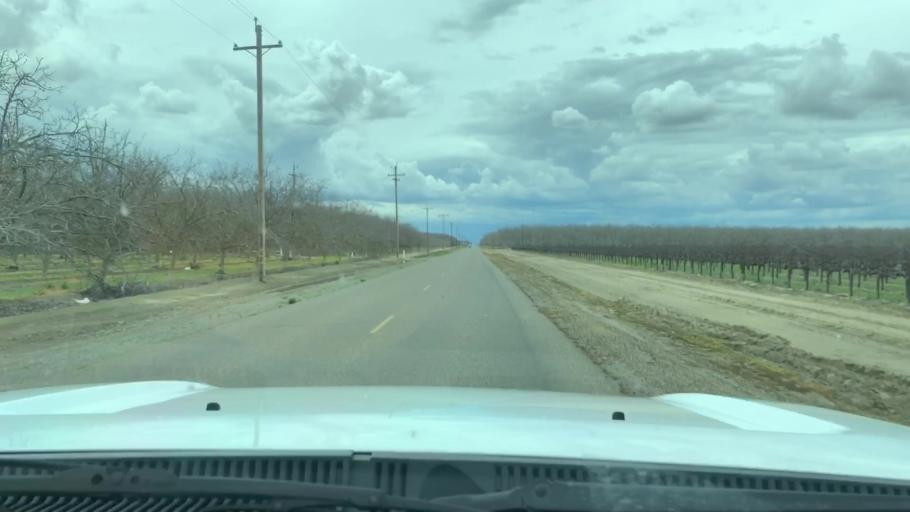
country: US
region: California
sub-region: Fresno County
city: Laton
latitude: 36.4894
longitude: -119.7516
